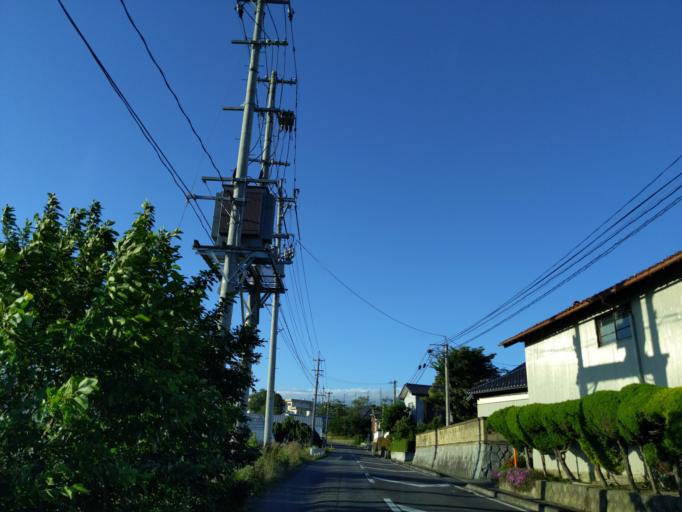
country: JP
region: Fukushima
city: Koriyama
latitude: 37.4006
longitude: 140.4118
